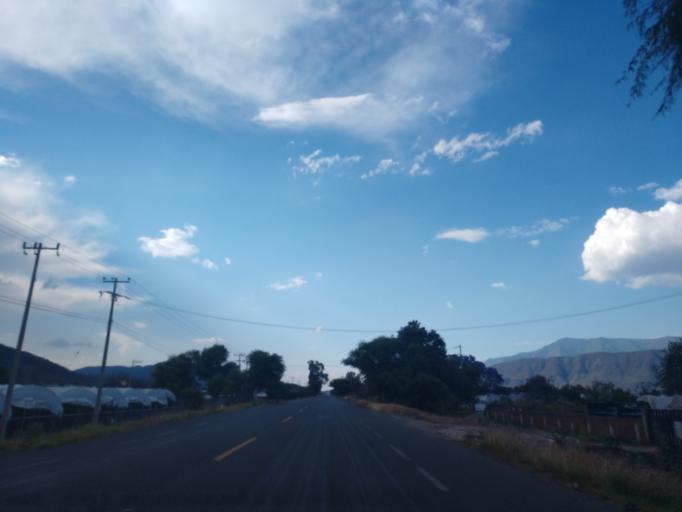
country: MX
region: Jalisco
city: Jocotepec
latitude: 20.2375
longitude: -103.4241
